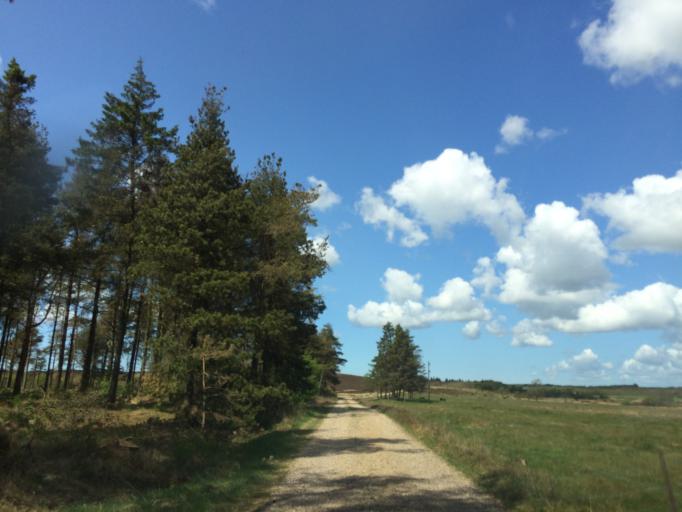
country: DK
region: Central Jutland
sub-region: Holstebro Kommune
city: Ulfborg
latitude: 56.2806
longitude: 8.4646
